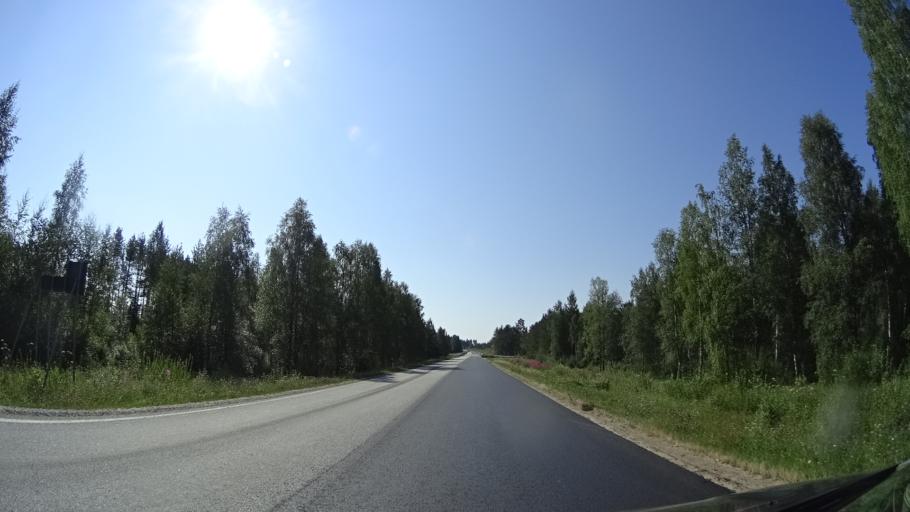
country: FI
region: North Karelia
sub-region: Joensuu
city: Juuka
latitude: 63.2363
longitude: 29.2832
